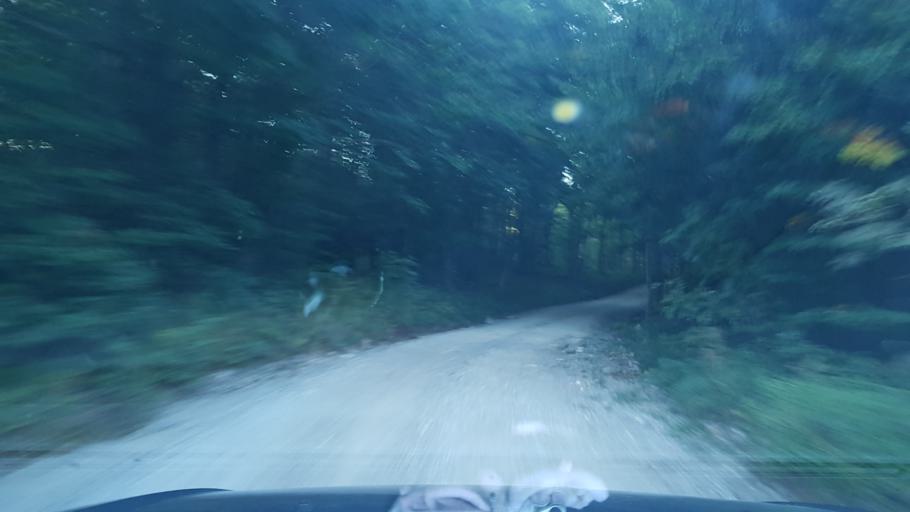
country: SI
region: Vipava
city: Vipava
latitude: 45.7738
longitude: 14.0494
